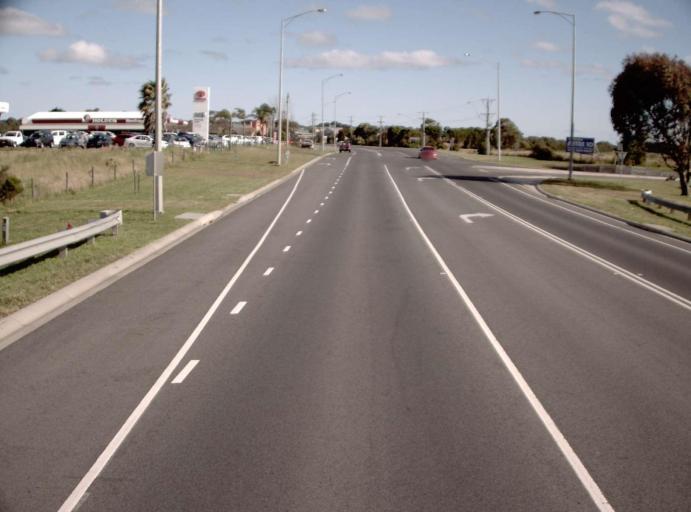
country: AU
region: Victoria
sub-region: Bass Coast
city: North Wonthaggi
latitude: -38.5833
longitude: 145.5758
